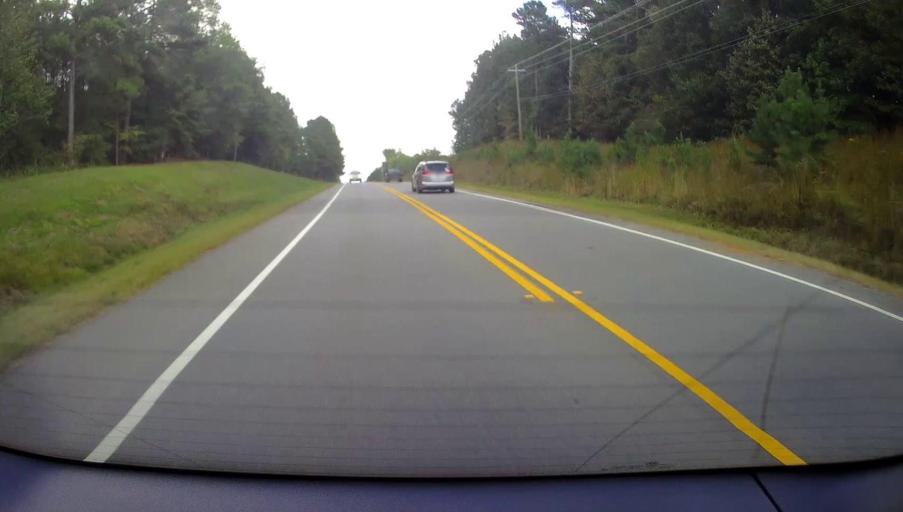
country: US
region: Georgia
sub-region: Baldwin County
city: Milledgeville
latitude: 33.0797
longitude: -83.3035
